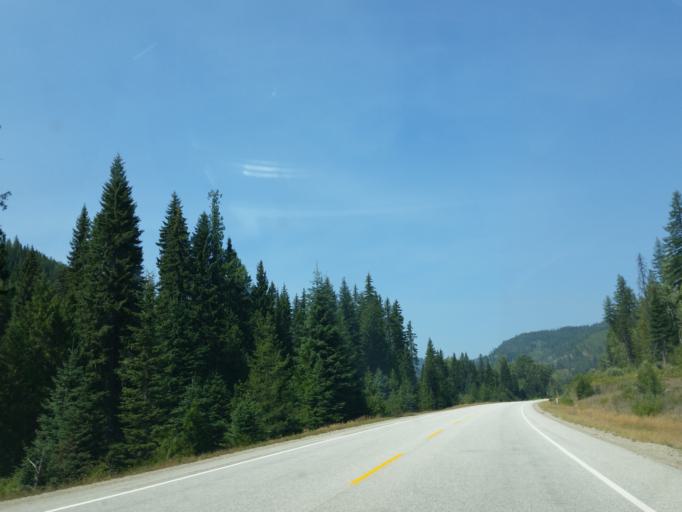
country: CA
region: British Columbia
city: Castlegar
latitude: 49.2959
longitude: -117.8246
